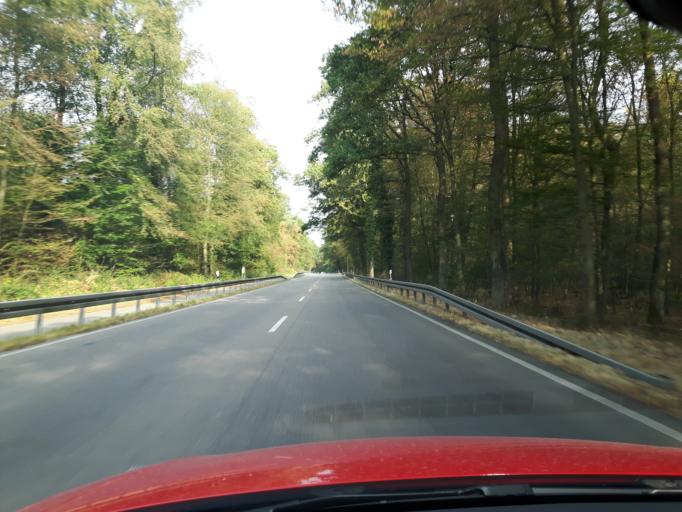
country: DE
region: Baden-Wuerttemberg
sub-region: Karlsruhe Region
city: Ettlingen
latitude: 48.9526
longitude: 8.3631
